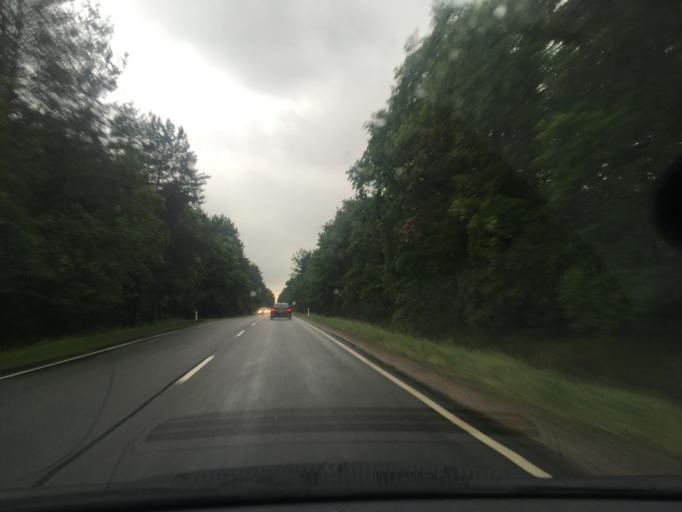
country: PL
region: Lublin Voivodeship
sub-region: Powiat rycki
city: Ryki
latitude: 51.5815
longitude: 21.9169
